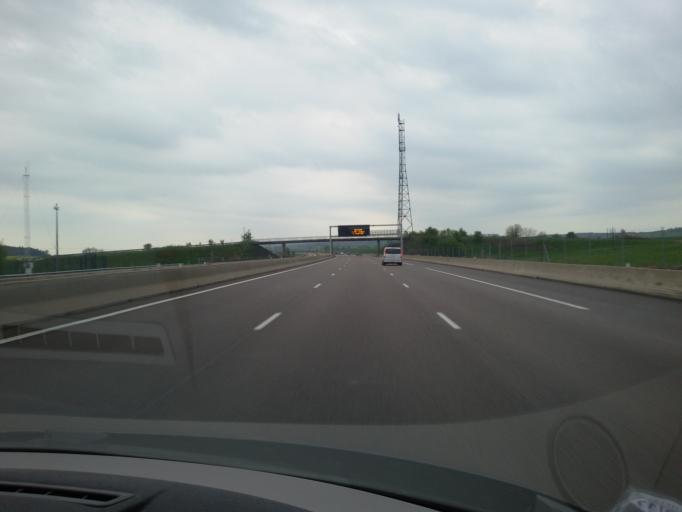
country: FR
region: Champagne-Ardenne
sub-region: Departement de la Haute-Marne
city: Rolampont
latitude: 47.8853
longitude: 5.2226
